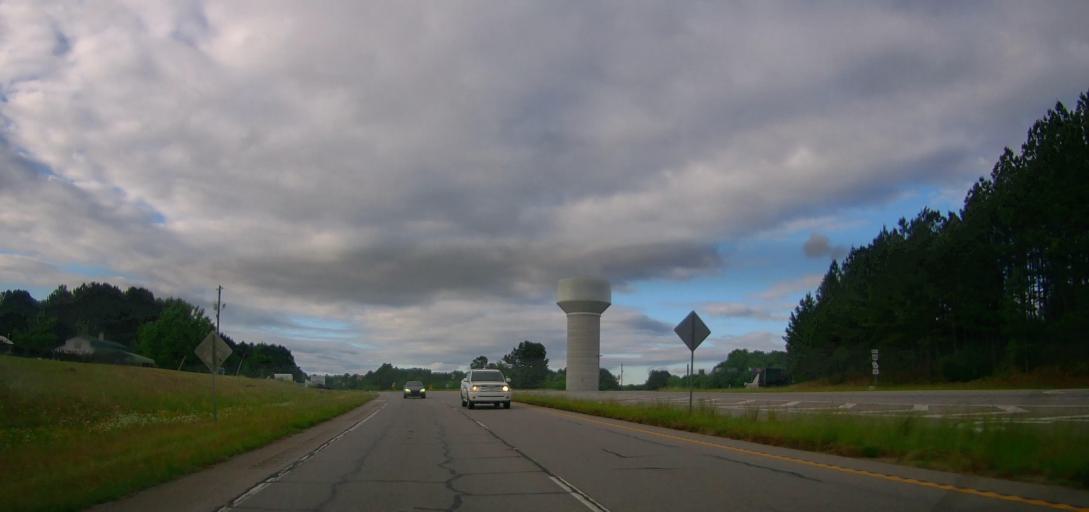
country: US
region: Georgia
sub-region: Oconee County
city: Watkinsville
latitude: 33.8449
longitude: -83.4235
